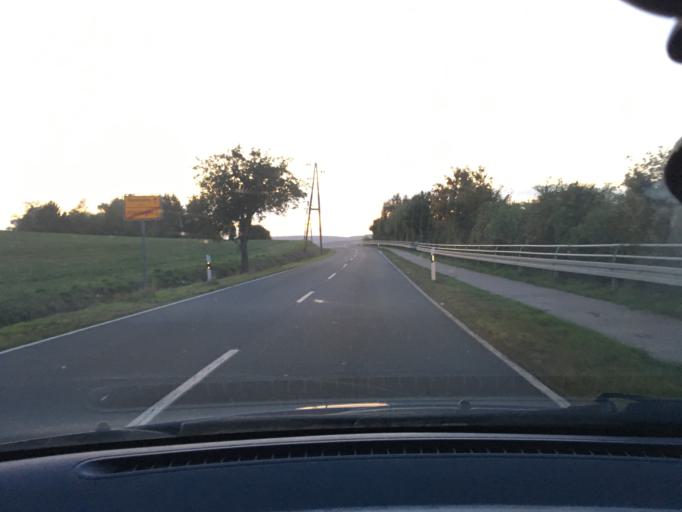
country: DE
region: Lower Saxony
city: Messenkamp
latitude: 52.2610
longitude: 9.3970
